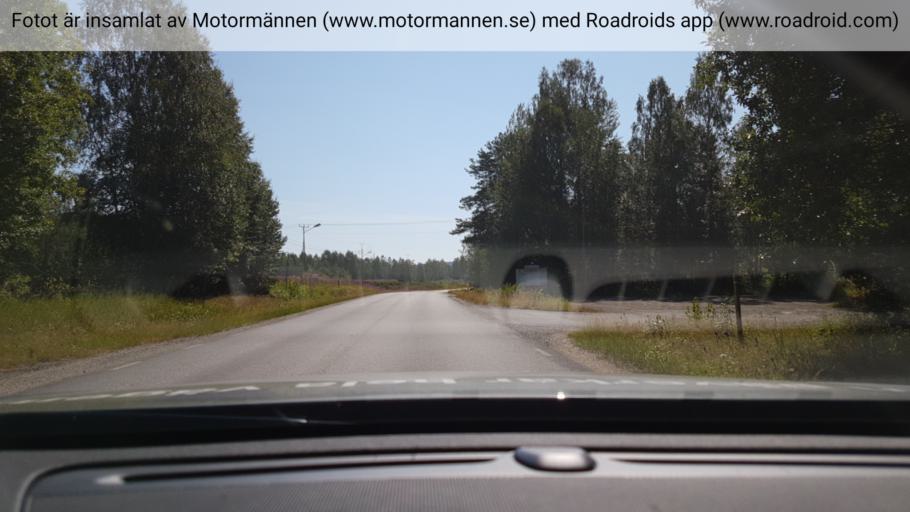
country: SE
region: Vaesterbotten
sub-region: Vindelns Kommun
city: Vindeln
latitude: 64.2162
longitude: 19.7104
